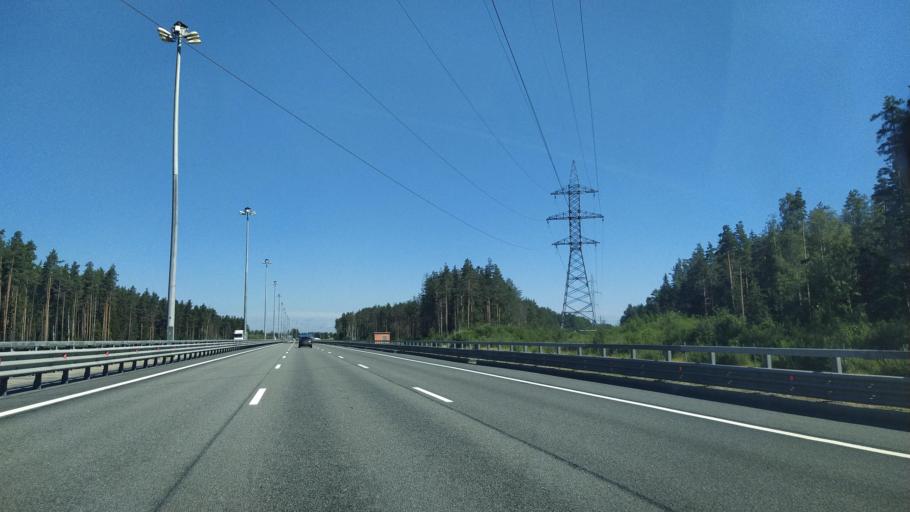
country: RU
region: St.-Petersburg
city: Bol'shaya Izhora
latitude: 59.9026
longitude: 29.6606
